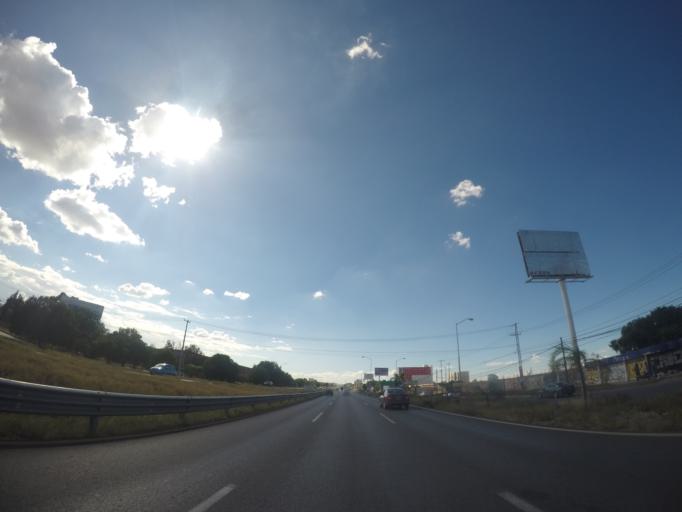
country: MX
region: San Luis Potosi
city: La Pila
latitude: 22.1086
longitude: -100.8928
